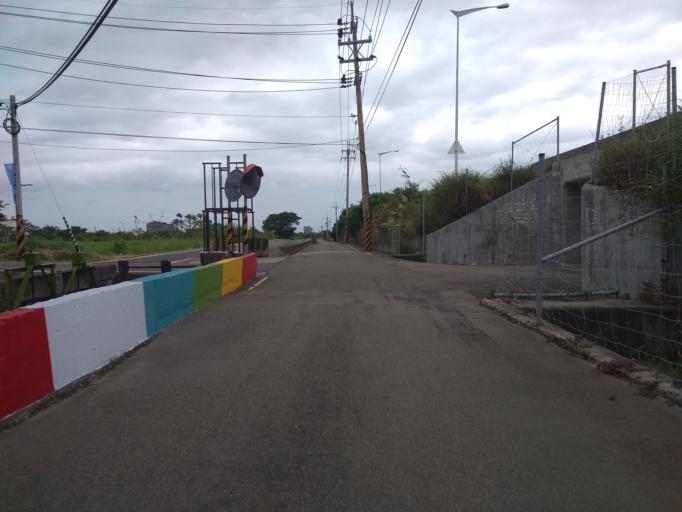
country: TW
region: Taiwan
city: Taoyuan City
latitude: 25.0443
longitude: 121.2194
